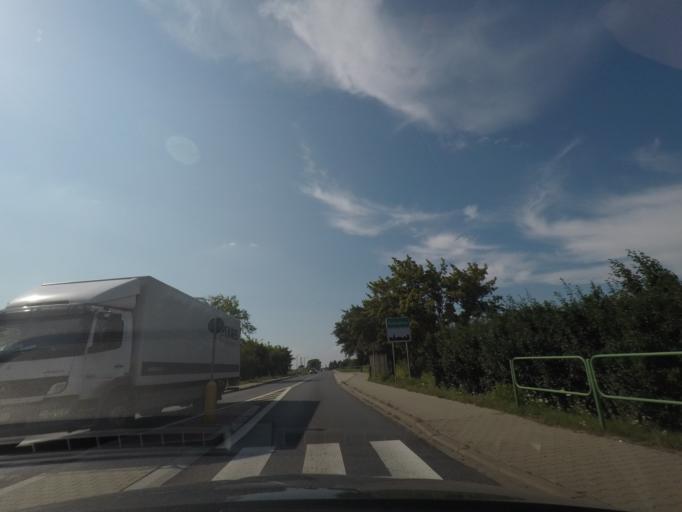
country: PL
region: Silesian Voivodeship
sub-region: Powiat pszczynski
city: Radostowice
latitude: 50.0058
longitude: 18.8711
